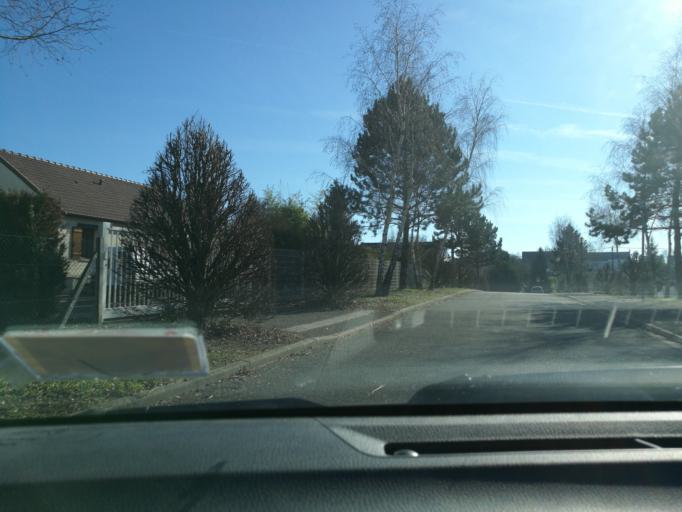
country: FR
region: Centre
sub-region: Departement du Loiret
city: Saint-Ay
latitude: 47.8631
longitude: 1.7554
